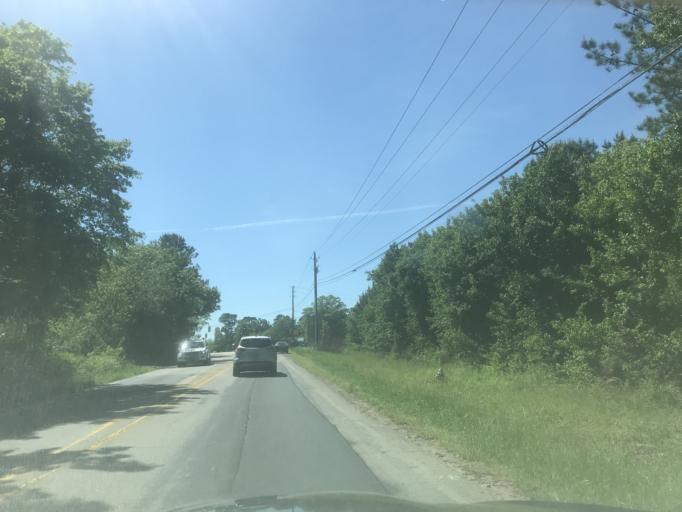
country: US
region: North Carolina
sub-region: Wake County
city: West Raleigh
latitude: 35.7429
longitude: -78.6784
